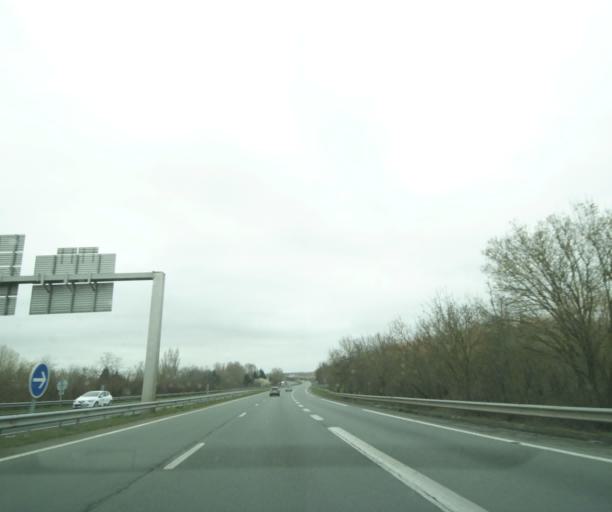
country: FR
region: Poitou-Charentes
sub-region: Departement de la Charente-Maritime
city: Breuil-Magne
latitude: 45.9699
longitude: -0.9841
